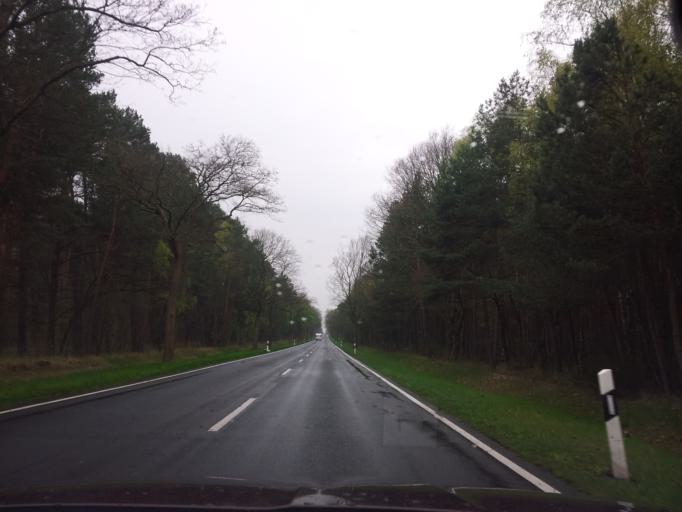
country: DE
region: Brandenburg
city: Treuenbrietzen
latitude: 52.0587
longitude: 12.8234
